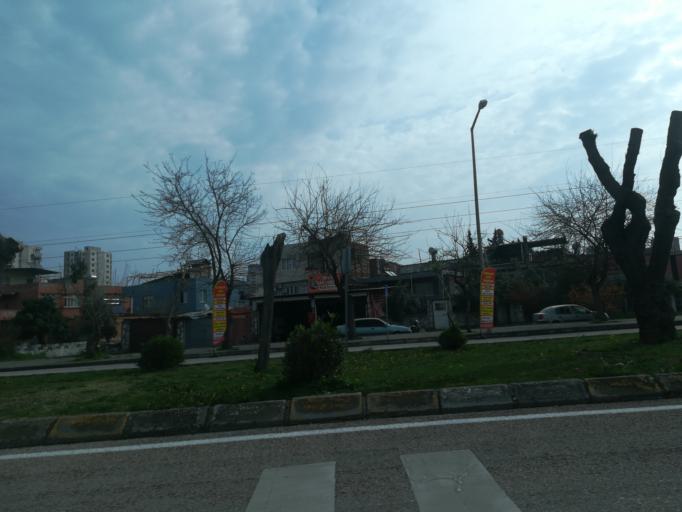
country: TR
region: Adana
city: Adana
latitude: 37.0057
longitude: 35.3555
